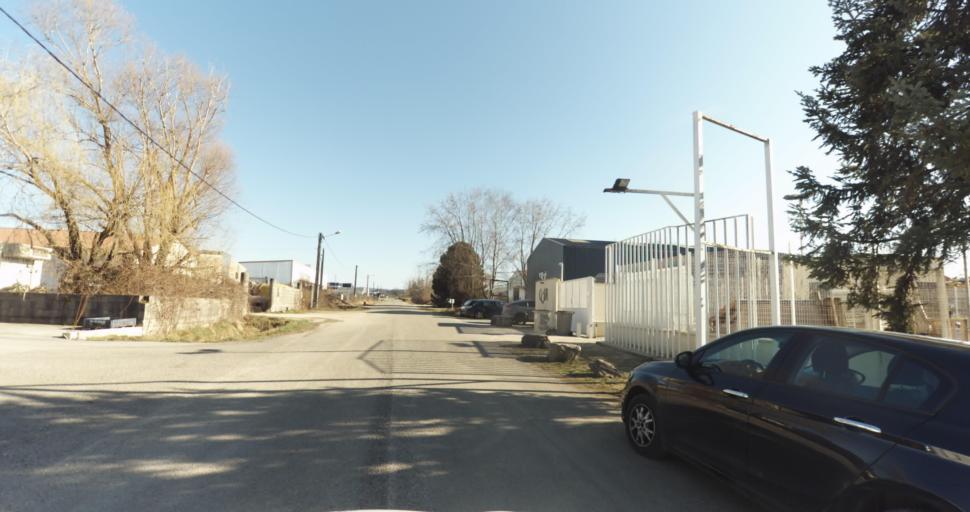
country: FR
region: Franche-Comte
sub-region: Departement du Jura
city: Montmorot
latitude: 46.6904
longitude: 5.5021
